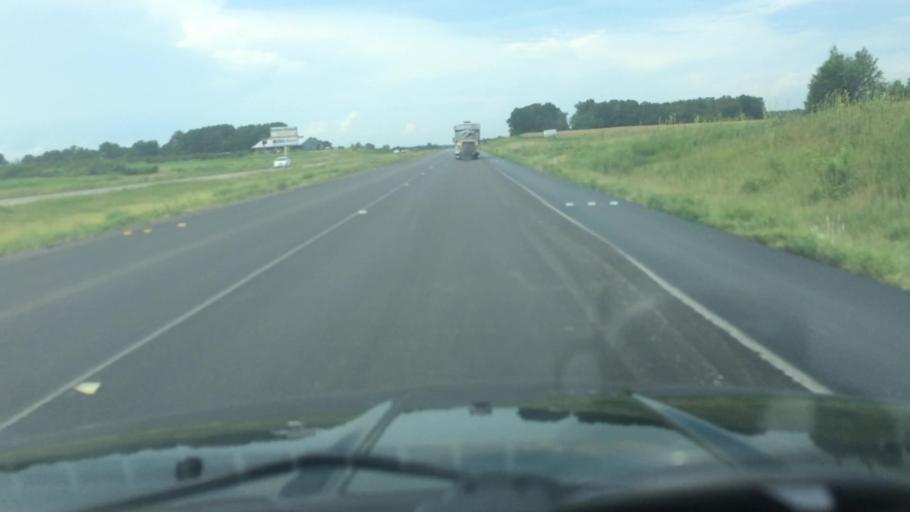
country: US
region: Missouri
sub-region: Saint Clair County
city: Osceola
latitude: 37.9766
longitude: -93.6480
